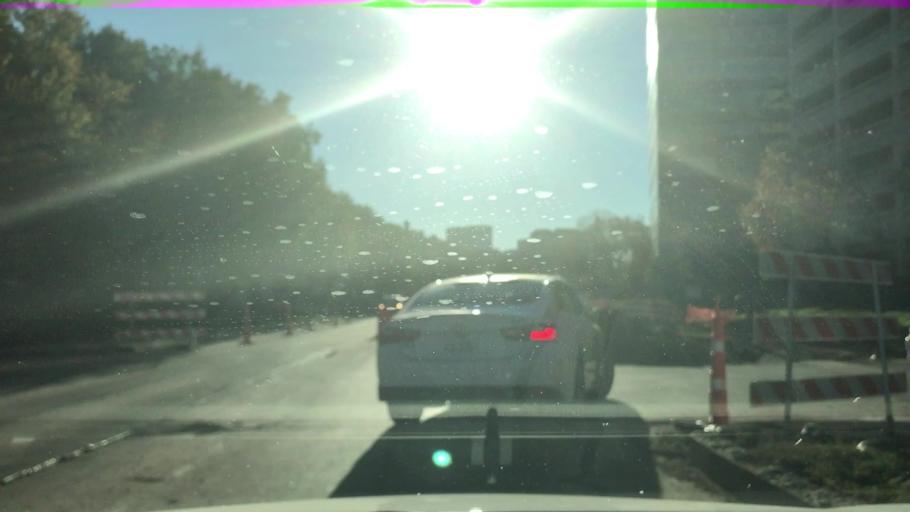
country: US
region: Texas
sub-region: Dallas County
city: Irving
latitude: 32.8675
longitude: -96.9395
